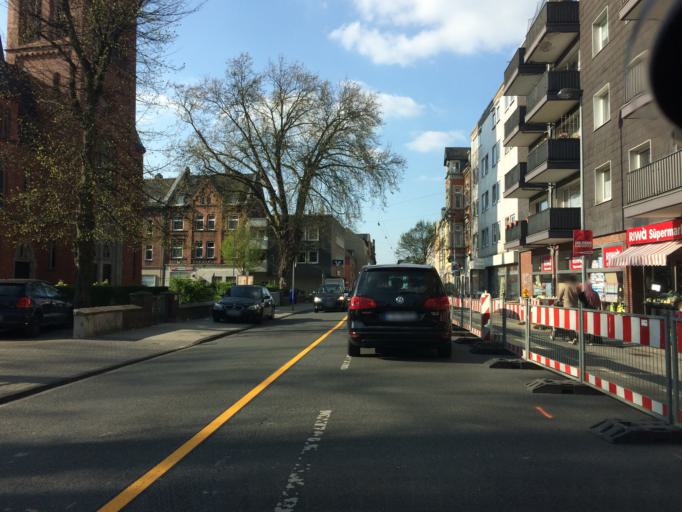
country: DE
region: North Rhine-Westphalia
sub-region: Regierungsbezirk Munster
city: Gelsenkirchen
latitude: 51.4997
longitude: 7.1199
